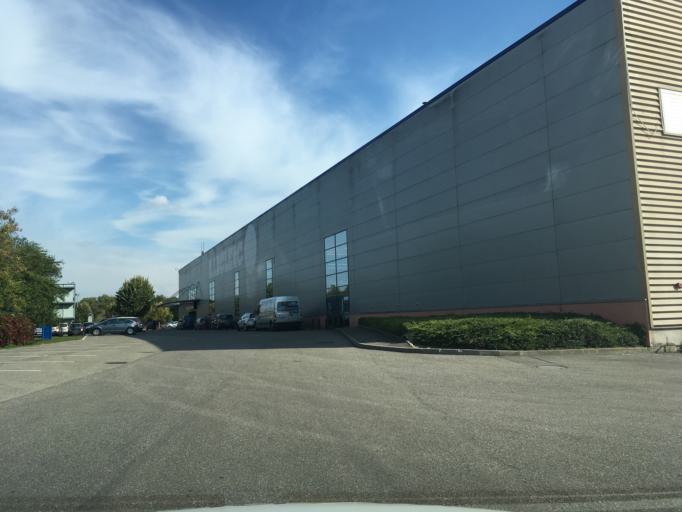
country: FR
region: Alsace
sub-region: Departement du Haut-Rhin
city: Colmar
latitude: 48.0816
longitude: 7.3793
